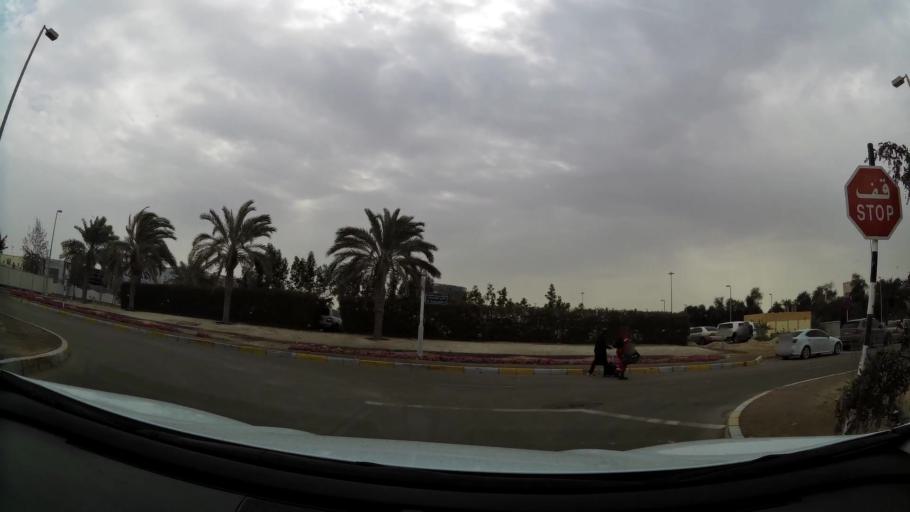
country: AE
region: Abu Dhabi
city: Abu Dhabi
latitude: 24.4260
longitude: 54.4526
